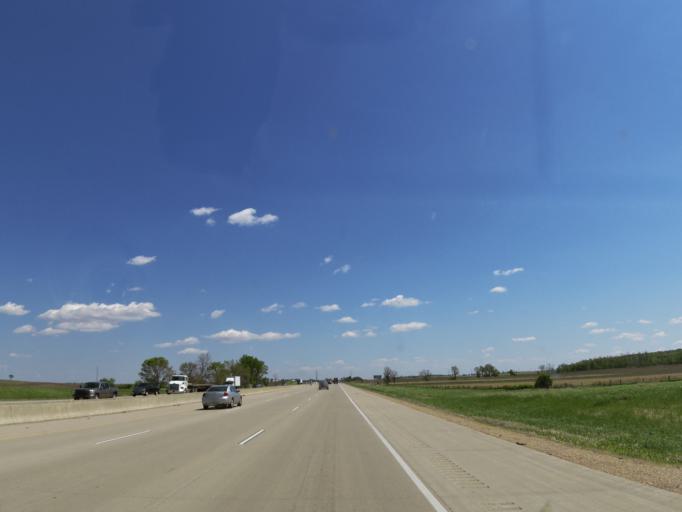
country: US
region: Wisconsin
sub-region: Dane County
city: De Forest
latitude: 43.2963
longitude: -89.4202
